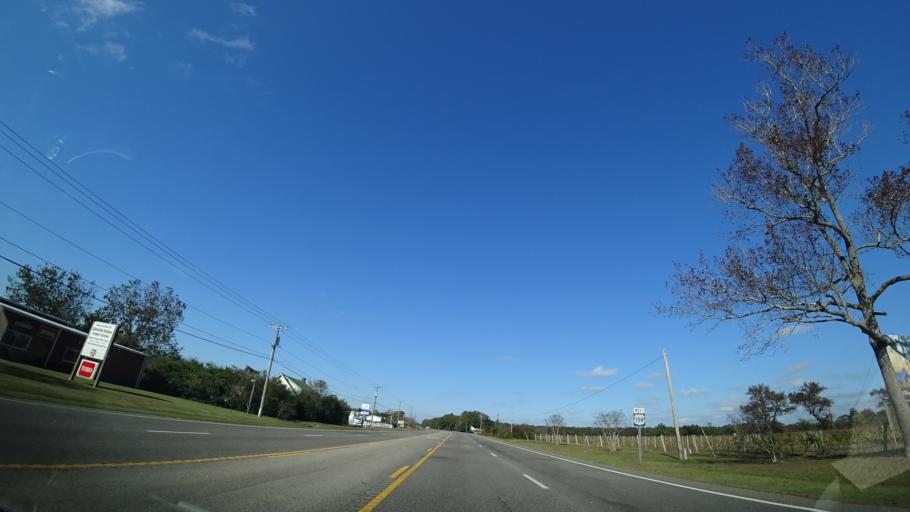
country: US
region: North Carolina
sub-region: Dare County
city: Southern Shores
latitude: 36.2116
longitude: -75.8659
